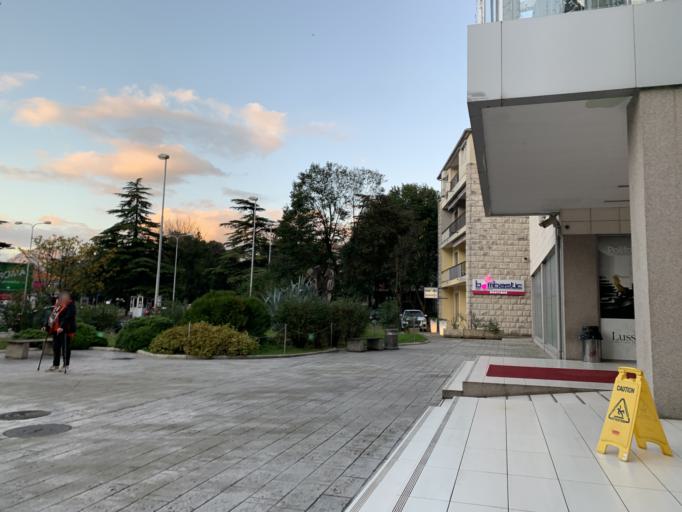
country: ME
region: Kotor
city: Kotor
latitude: 42.4279
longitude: 18.7698
